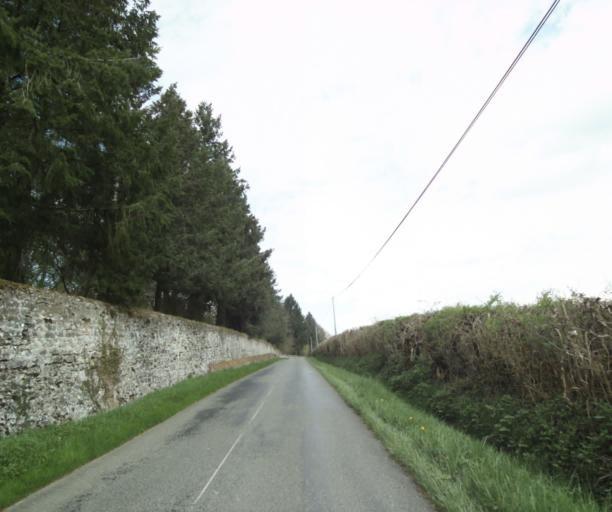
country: FR
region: Bourgogne
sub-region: Departement de Saone-et-Loire
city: Palinges
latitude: 46.5343
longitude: 4.2131
